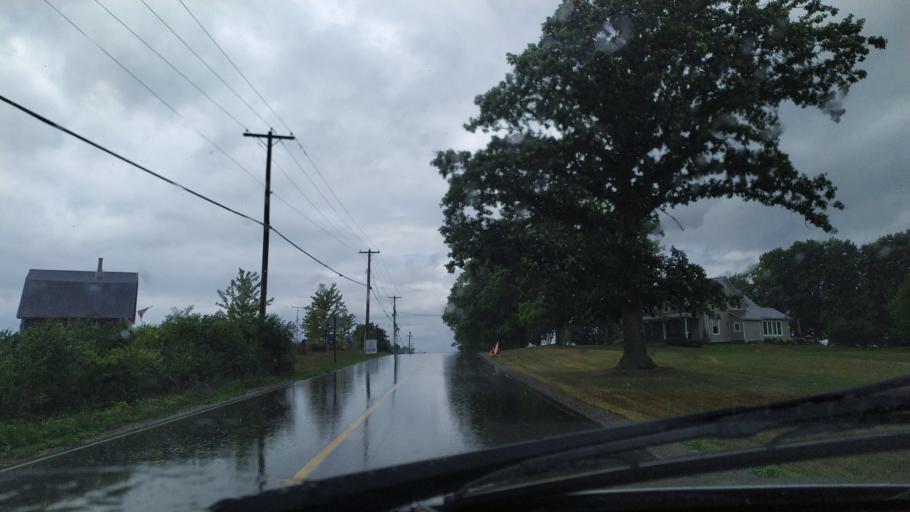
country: CA
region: Ontario
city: Prince Edward
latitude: 43.9713
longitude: -77.4260
